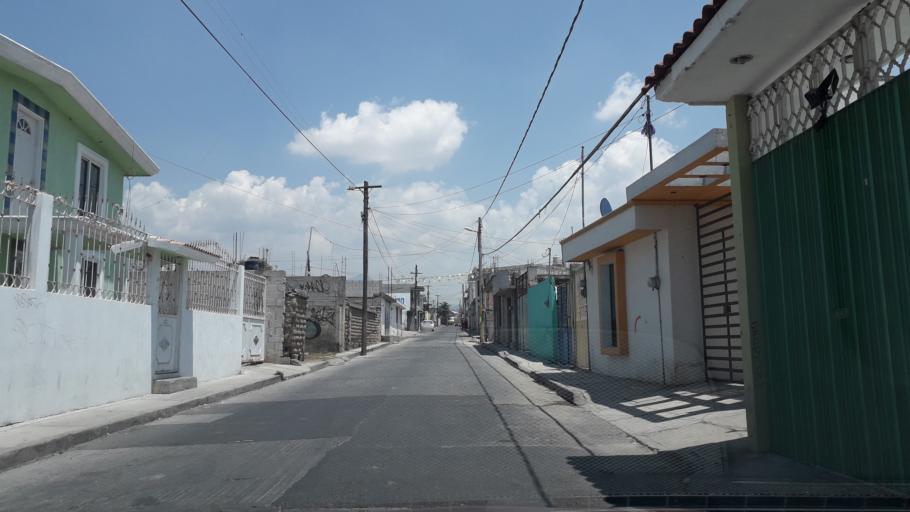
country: MX
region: Puebla
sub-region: Puebla
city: Santa Maria Xonacatepec
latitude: 19.0866
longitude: -98.1029
